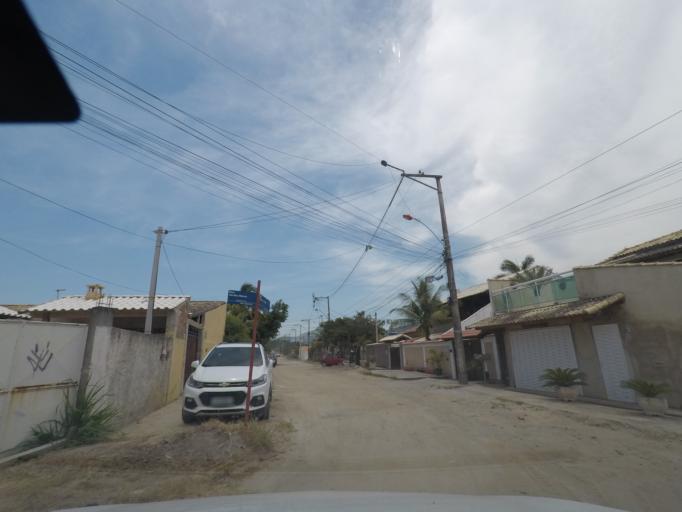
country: BR
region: Rio de Janeiro
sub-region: Niteroi
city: Niteroi
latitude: -22.9621
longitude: -42.9711
